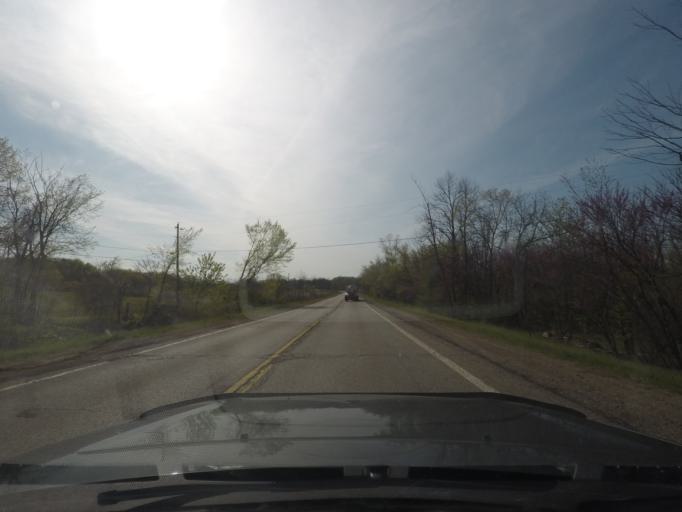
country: US
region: Michigan
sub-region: Berrien County
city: Buchanan
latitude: 41.7956
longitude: -86.4525
